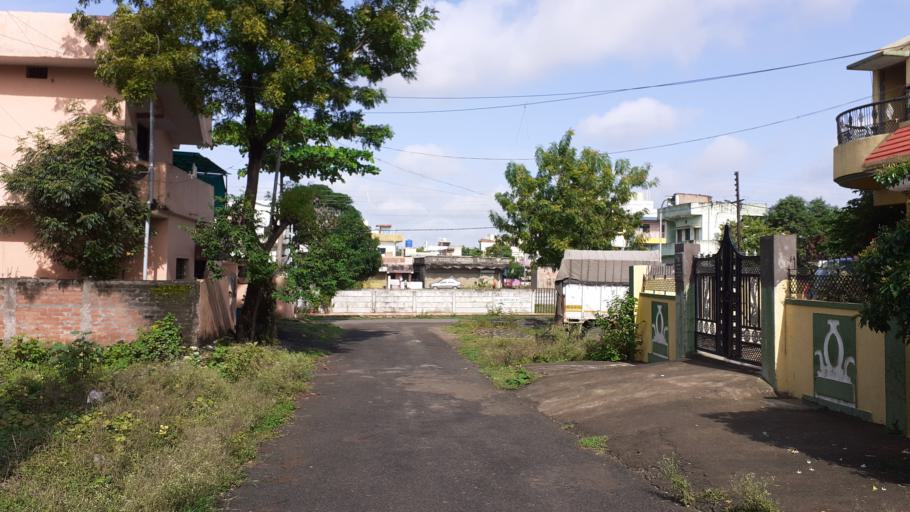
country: IN
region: Maharashtra
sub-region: Nagpur Division
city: Nagpur
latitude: 21.0975
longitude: 79.1095
